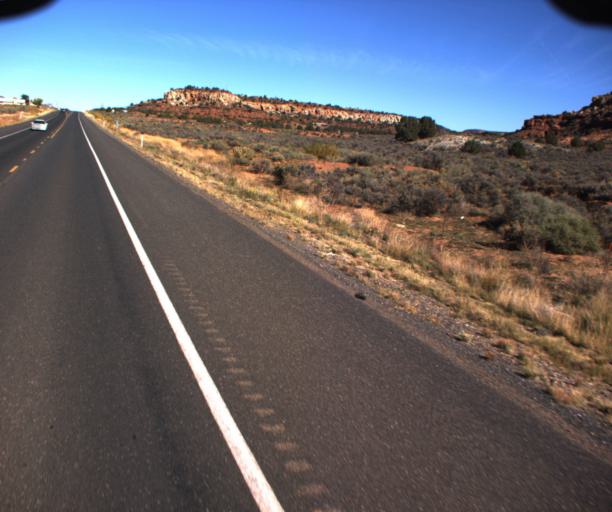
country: US
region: Arizona
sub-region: Coconino County
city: Fredonia
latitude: 36.9842
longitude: -112.5297
